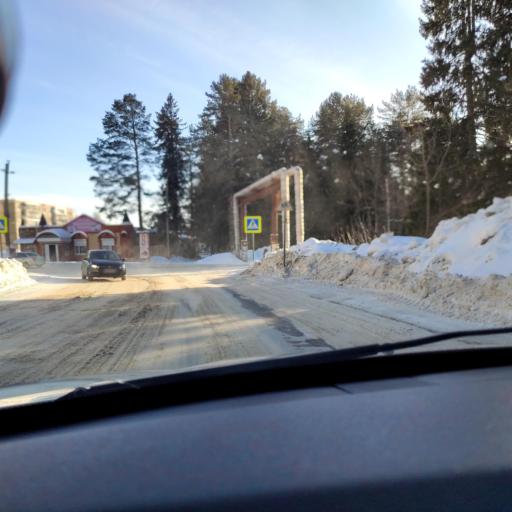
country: RU
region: Perm
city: Dobryanka
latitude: 58.4707
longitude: 56.3944
